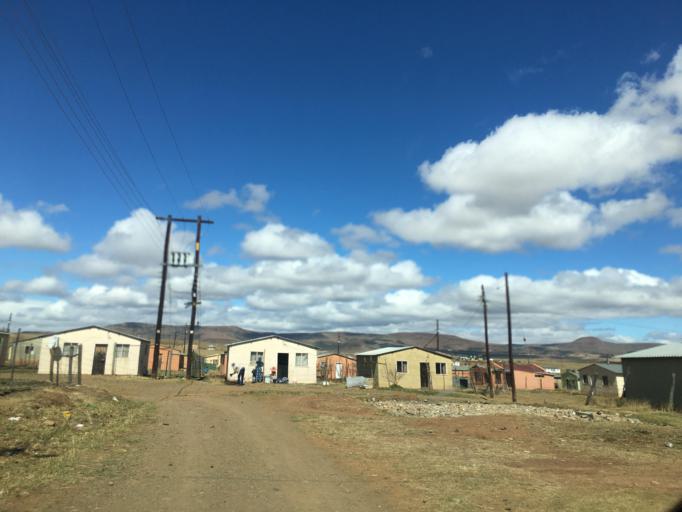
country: ZA
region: Eastern Cape
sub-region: Chris Hani District Municipality
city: Cala
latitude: -31.5407
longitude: 27.6788
